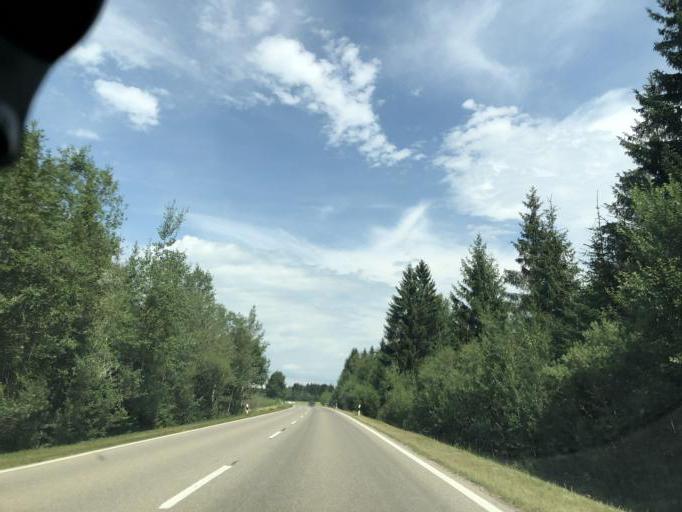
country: DE
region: Bavaria
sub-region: Swabia
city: Wertach
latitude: 47.6075
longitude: 10.4278
